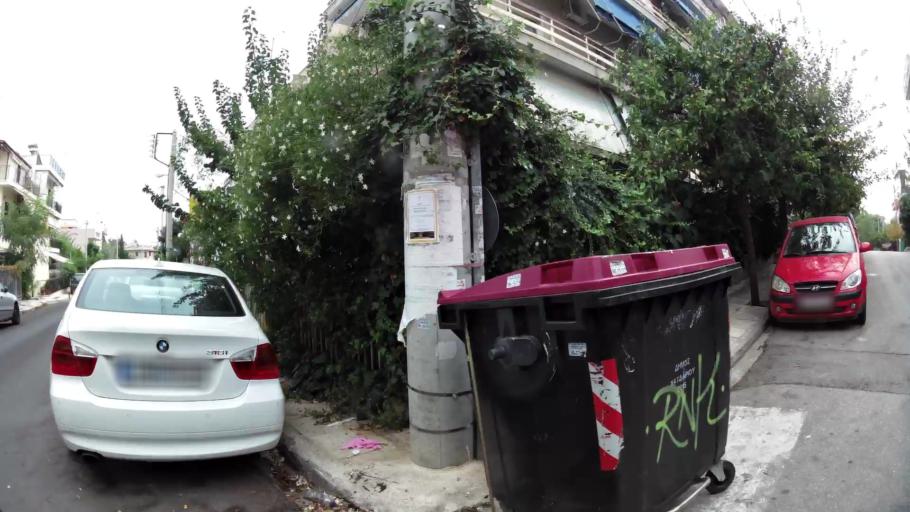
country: GR
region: Attica
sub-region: Nomarchia Athinas
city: Chaidari
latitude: 38.0002
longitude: 23.6653
